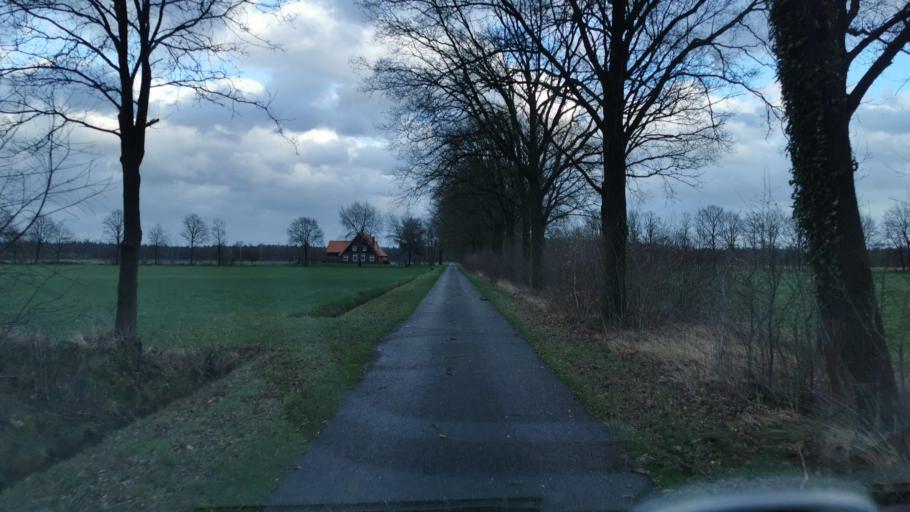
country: DE
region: Lower Saxony
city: Lage
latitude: 52.4408
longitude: 6.9893
